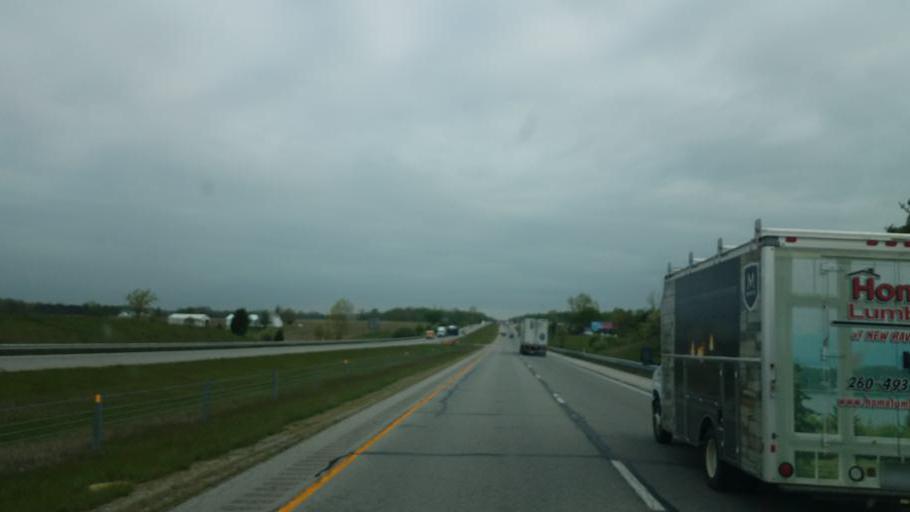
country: US
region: Indiana
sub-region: DeKalb County
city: Garrett
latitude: 41.2846
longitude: -85.0871
